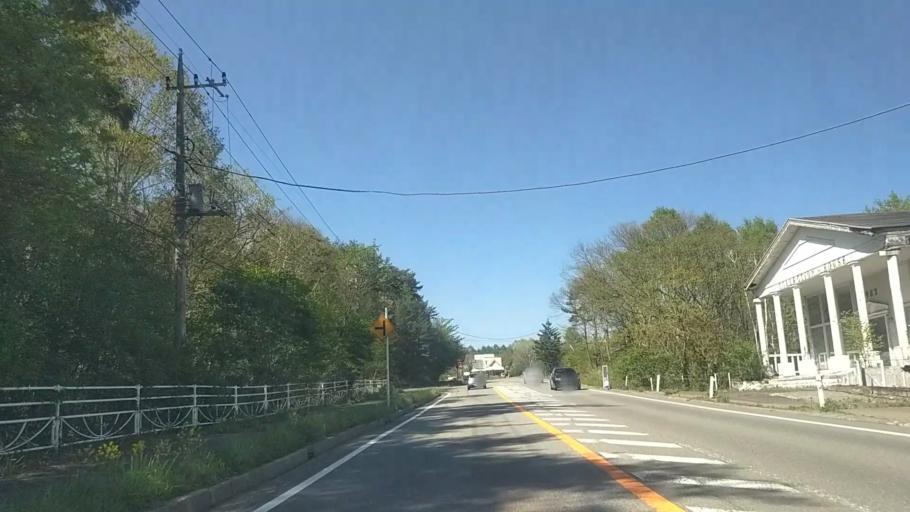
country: JP
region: Yamanashi
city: Nirasaki
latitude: 35.9272
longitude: 138.4417
